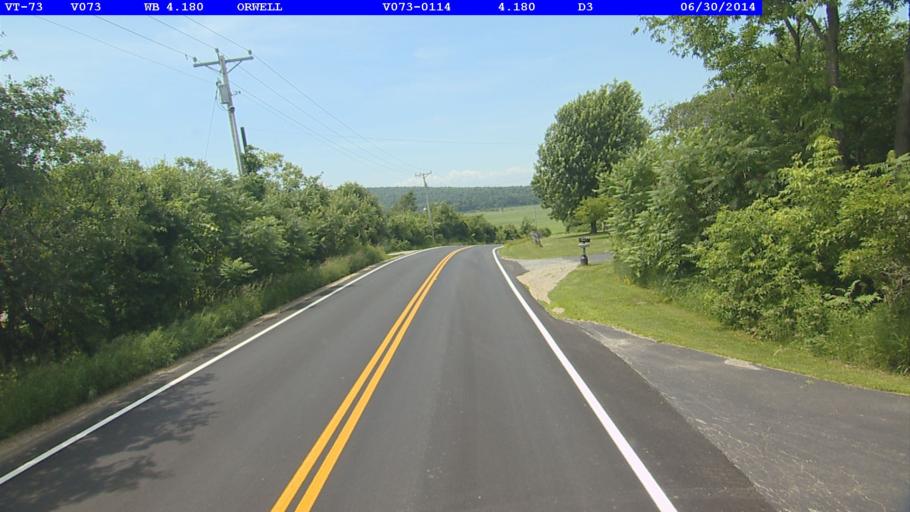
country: US
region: Vermont
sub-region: Rutland County
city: Brandon
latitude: 43.7957
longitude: -73.2270
